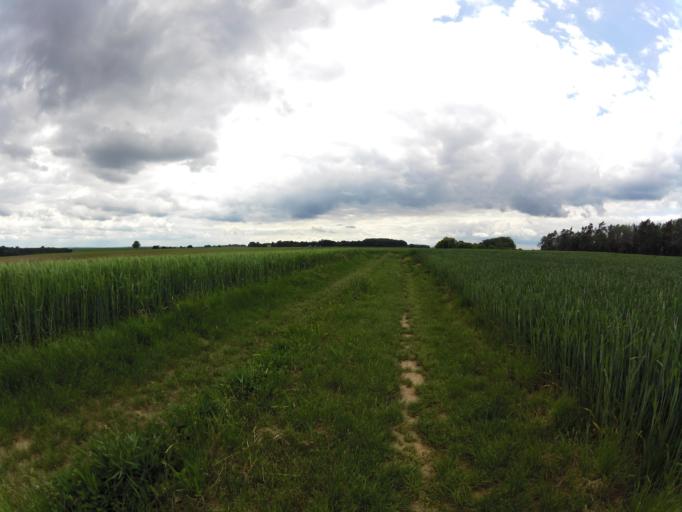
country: DE
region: Bavaria
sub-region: Regierungsbezirk Unterfranken
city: Gaukonigshofen
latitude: 49.6660
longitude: 9.9967
